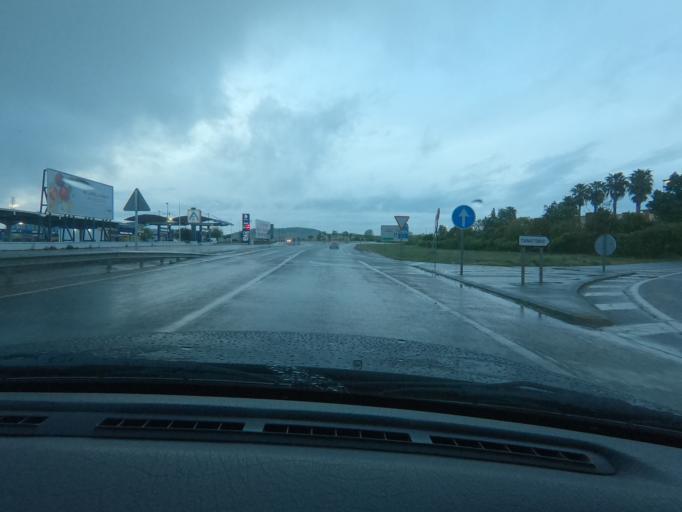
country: ES
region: Extremadura
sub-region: Provincia de Badajoz
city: Merida
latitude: 38.9346
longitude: -6.3435
